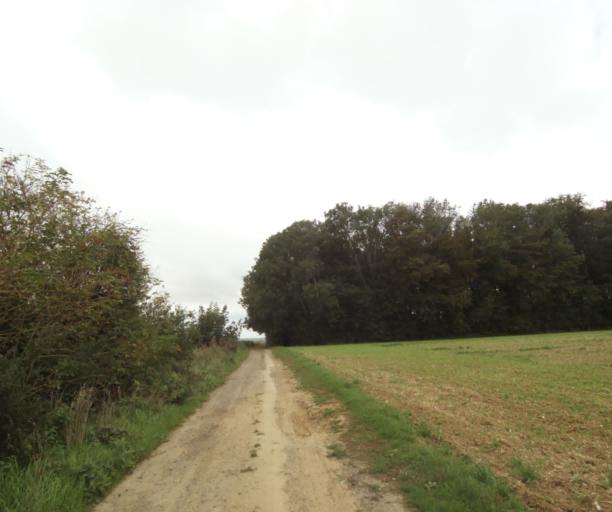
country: FR
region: Nord-Pas-de-Calais
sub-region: Departement du Pas-de-Calais
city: Etaples
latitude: 50.5276
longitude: 1.6684
